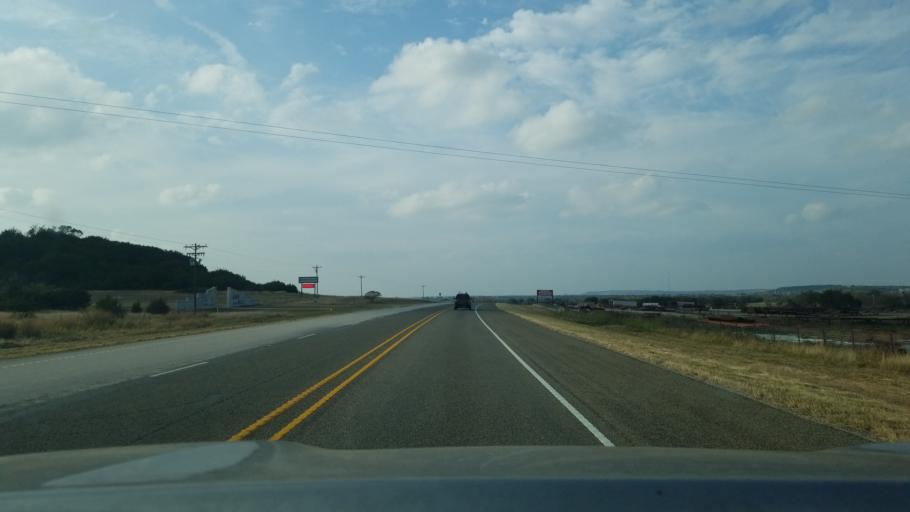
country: US
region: Texas
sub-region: Lampasas County
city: Lampasas
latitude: 31.1923
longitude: -98.3793
